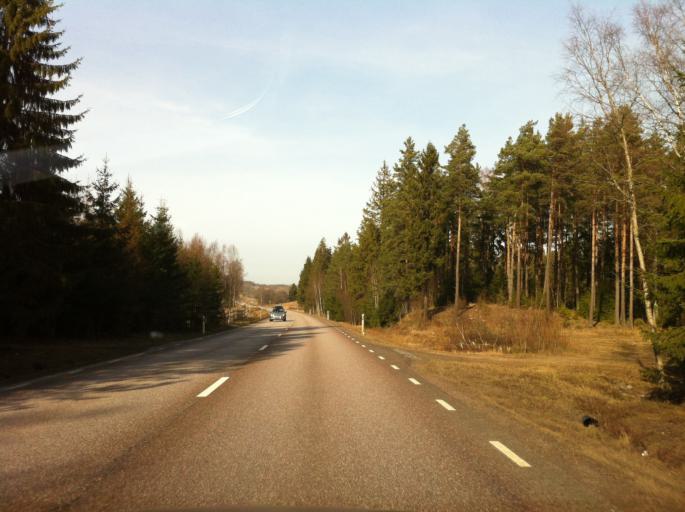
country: SE
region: Vaestra Goetaland
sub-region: Skovde Kommun
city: Skultorp
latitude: 58.2768
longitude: 13.8097
